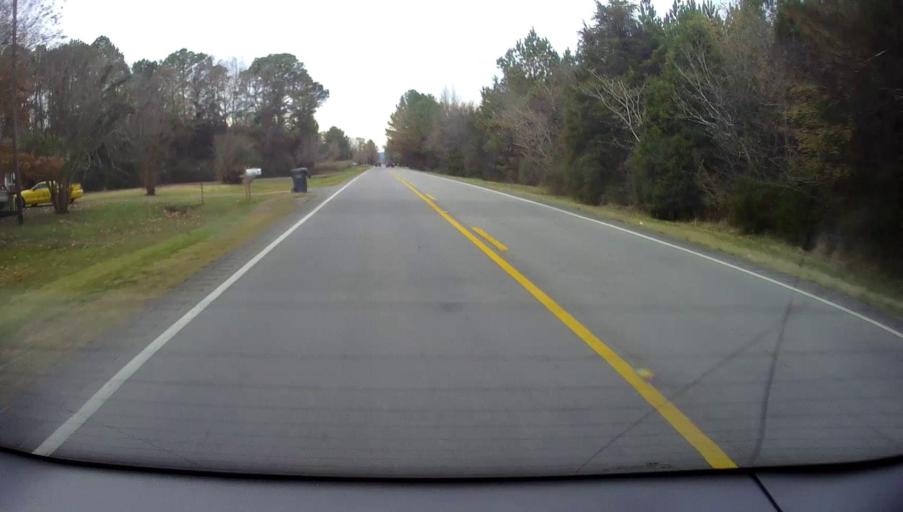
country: US
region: Alabama
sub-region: Marshall County
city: Arab
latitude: 34.3900
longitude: -86.6691
